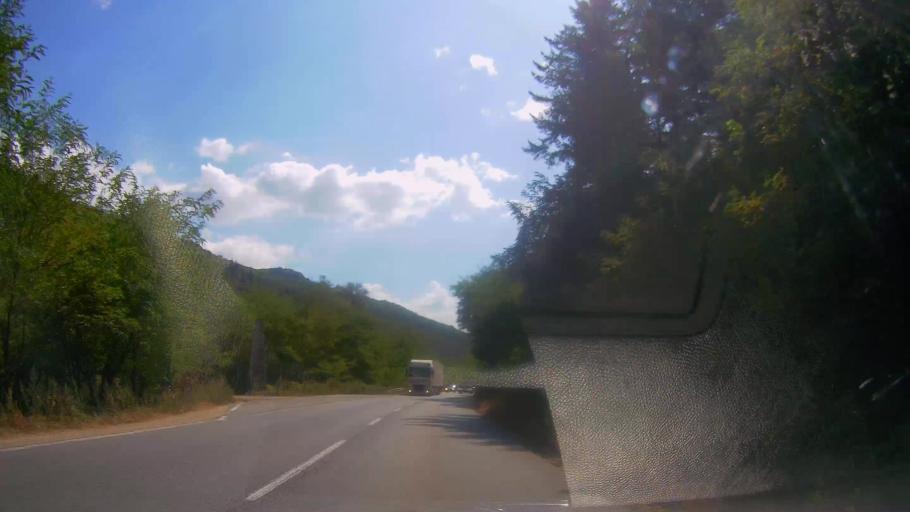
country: BG
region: Stara Zagora
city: Gurkovo
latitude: 42.7576
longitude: 25.7078
